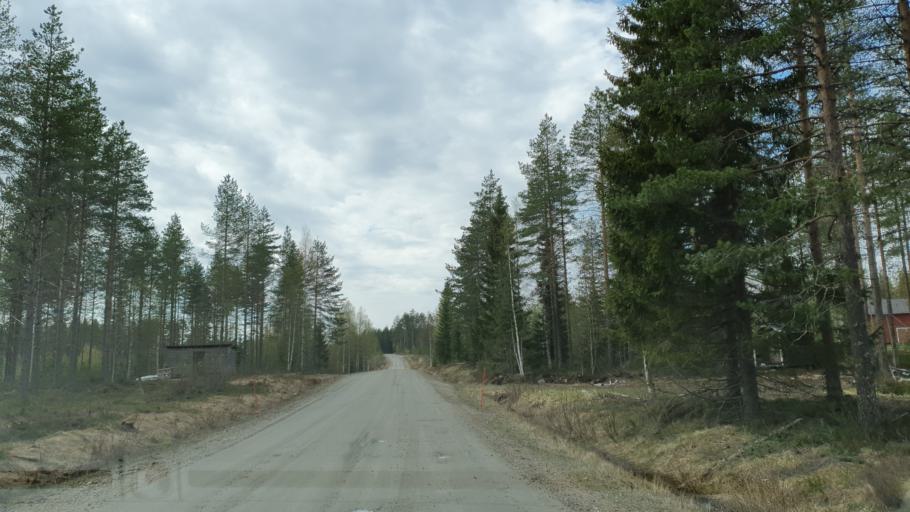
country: FI
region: Kainuu
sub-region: Kehys-Kainuu
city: Kuhmo
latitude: 64.0954
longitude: 29.9023
